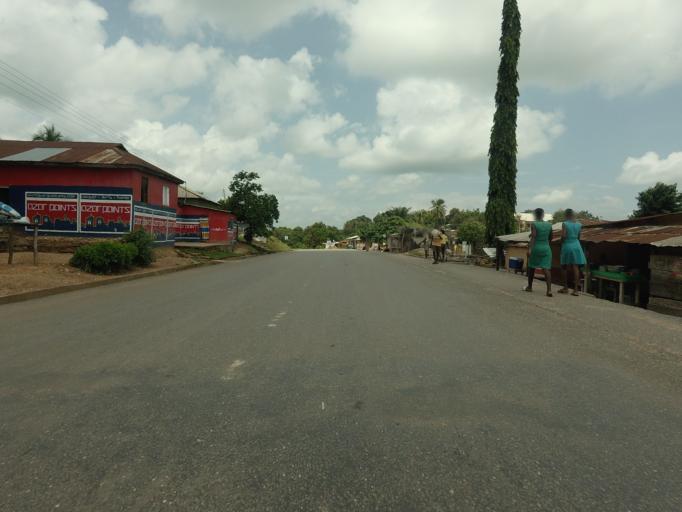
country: GH
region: Volta
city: Ho
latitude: 6.7383
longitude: 0.3487
